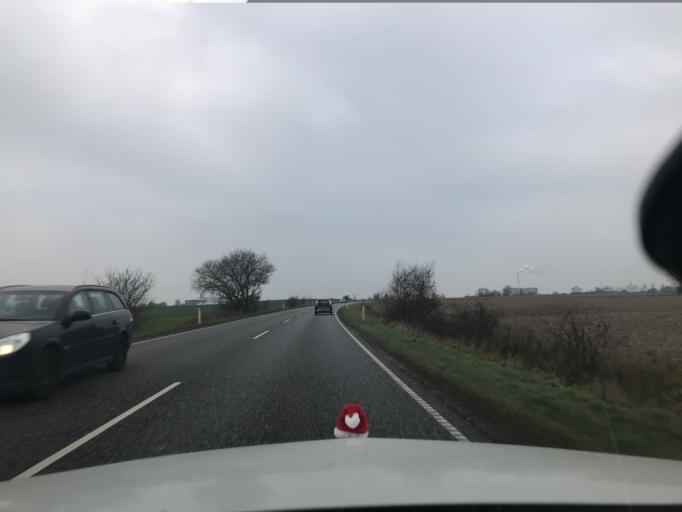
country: DK
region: South Denmark
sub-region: Sonderborg Kommune
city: Horuphav
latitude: 54.9225
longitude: 9.8777
